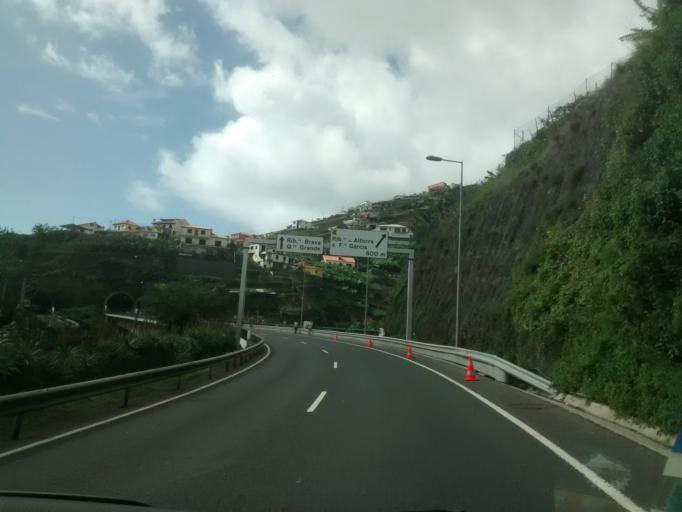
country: PT
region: Madeira
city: Camara de Lobos
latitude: 32.6622
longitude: -16.9804
